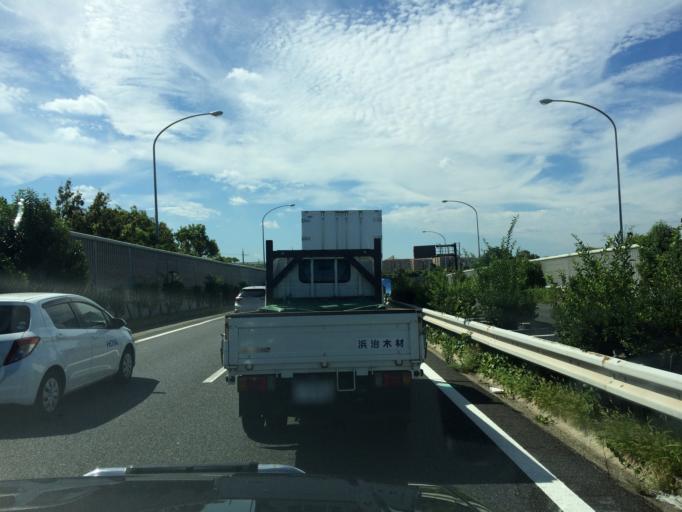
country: JP
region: Osaka
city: Takaishi
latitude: 34.5027
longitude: 135.4885
